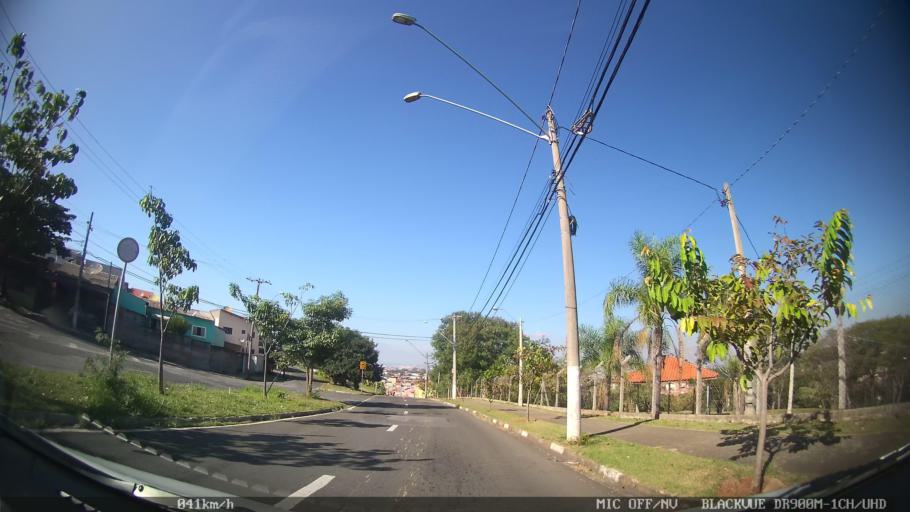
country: BR
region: Sao Paulo
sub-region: Campinas
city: Campinas
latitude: -22.9343
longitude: -47.1215
